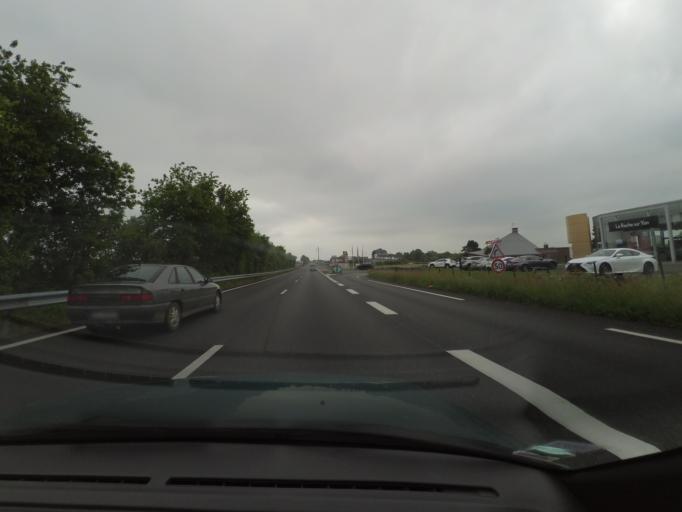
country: FR
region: Pays de la Loire
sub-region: Departement de la Vendee
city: Mouilleron-le-Captif
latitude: 46.7146
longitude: -1.4298
